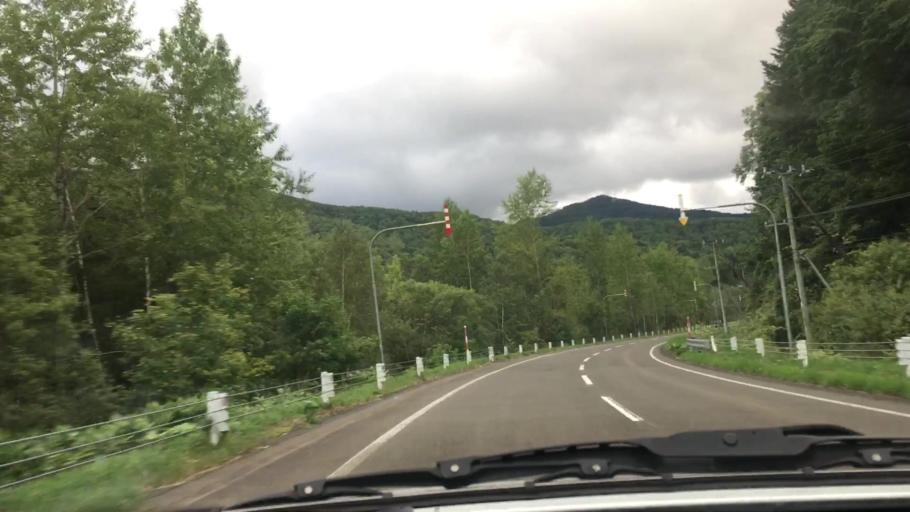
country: JP
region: Hokkaido
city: Shimo-furano
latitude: 43.0541
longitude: 142.5324
